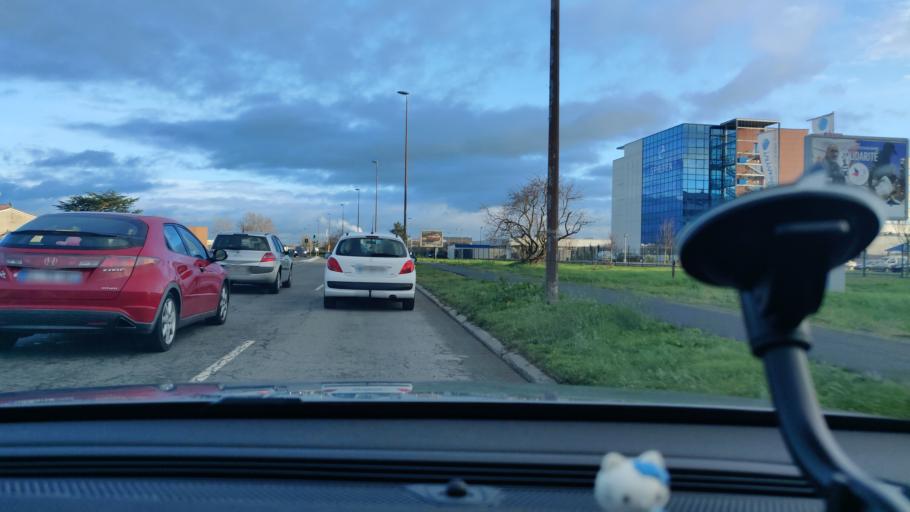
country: FR
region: Midi-Pyrenees
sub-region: Departement de la Haute-Garonne
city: Cugnaux
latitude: 43.5671
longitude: 1.3779
